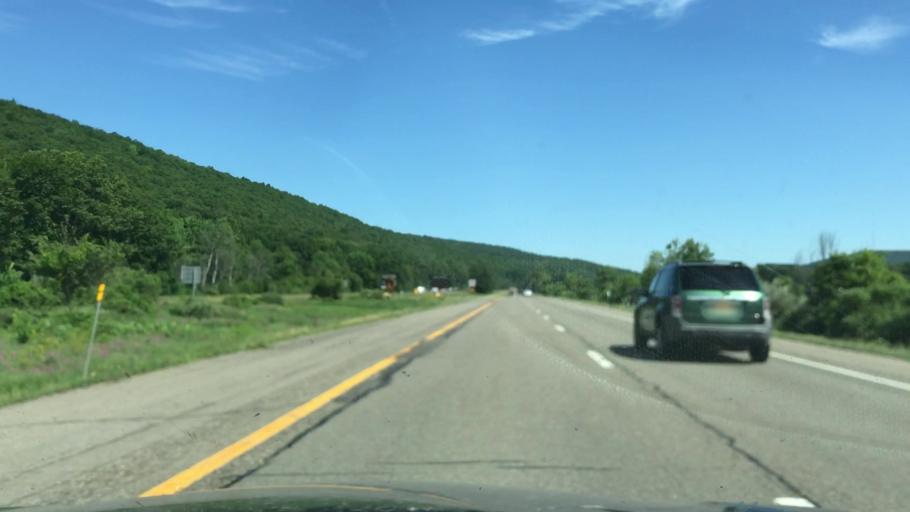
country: US
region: New York
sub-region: Steuben County
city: Painted Post
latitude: 42.1812
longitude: -77.1221
